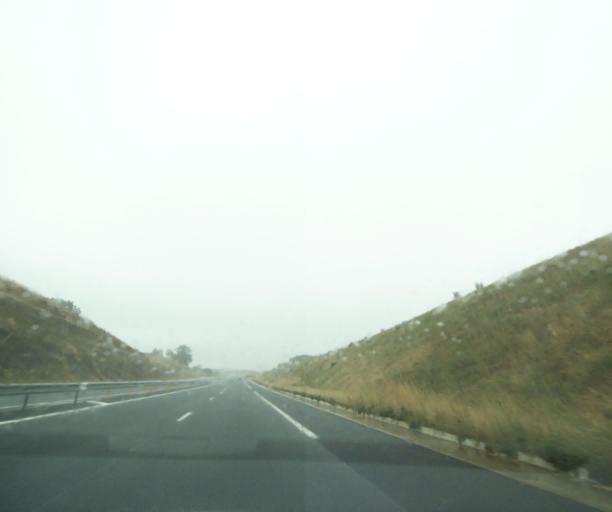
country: FR
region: Midi-Pyrenees
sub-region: Departement de l'Aveyron
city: Naucelle
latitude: 44.2068
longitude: 2.3981
